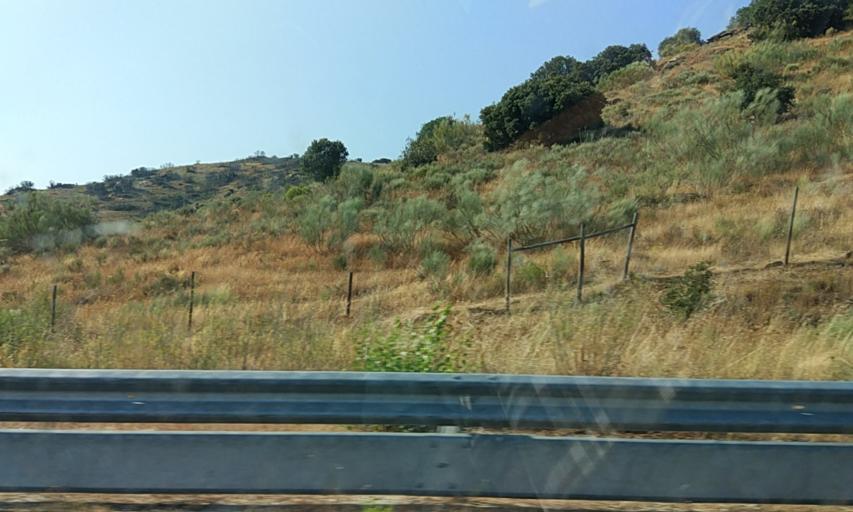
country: PT
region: Braganca
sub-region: Mirandela
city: Mirandela
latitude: 41.5207
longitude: -7.1250
